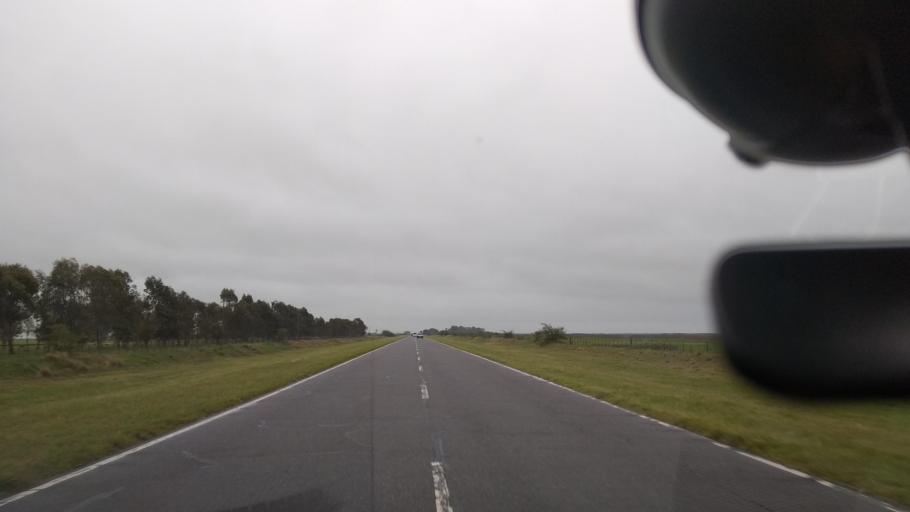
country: AR
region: Buenos Aires
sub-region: Partido de Dolores
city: Dolores
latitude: -36.0709
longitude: -57.4400
